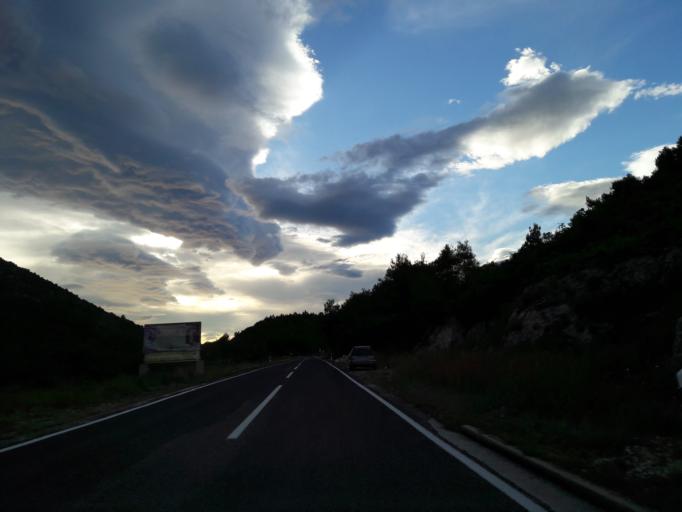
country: HR
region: Dubrovacko-Neretvanska
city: Ston
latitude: 42.8329
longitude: 17.6434
